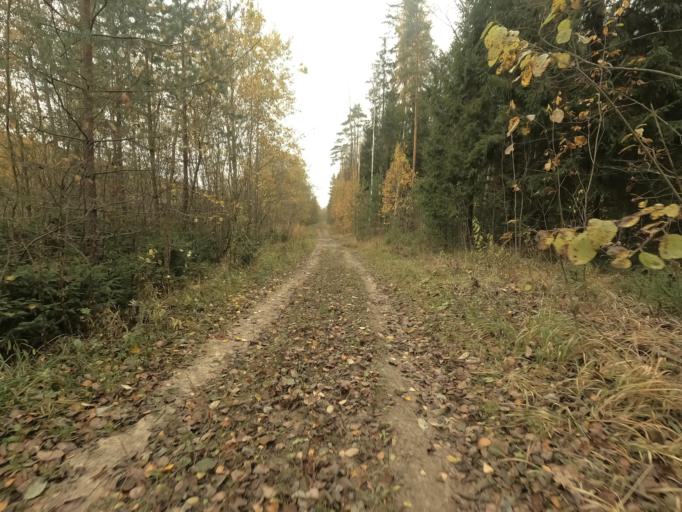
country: RU
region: Leningrad
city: Pavlovo
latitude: 59.7763
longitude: 30.9019
